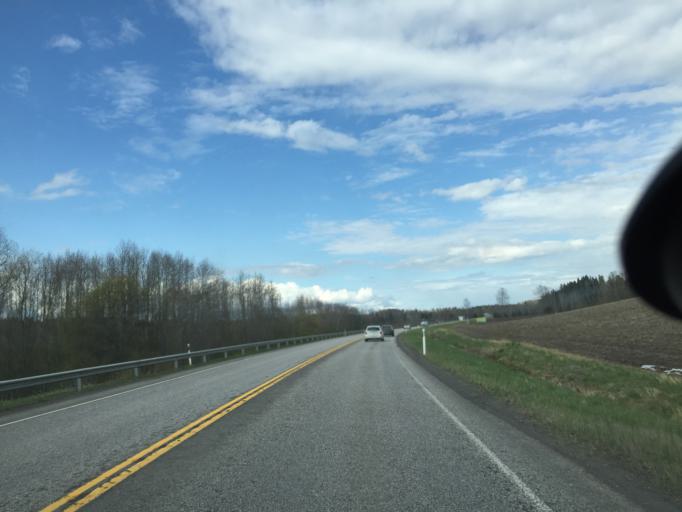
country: FI
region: Uusimaa
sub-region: Helsinki
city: Lohja
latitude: 60.1964
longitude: 24.0107
